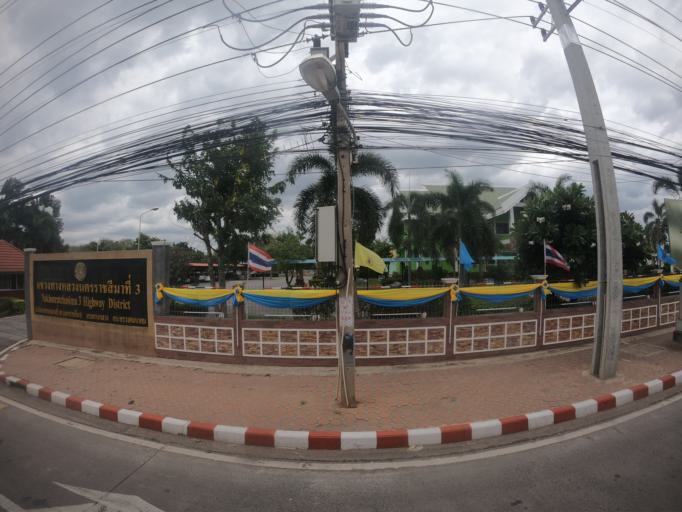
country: TH
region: Nakhon Ratchasima
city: Nakhon Ratchasima
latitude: 14.9162
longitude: 102.1487
